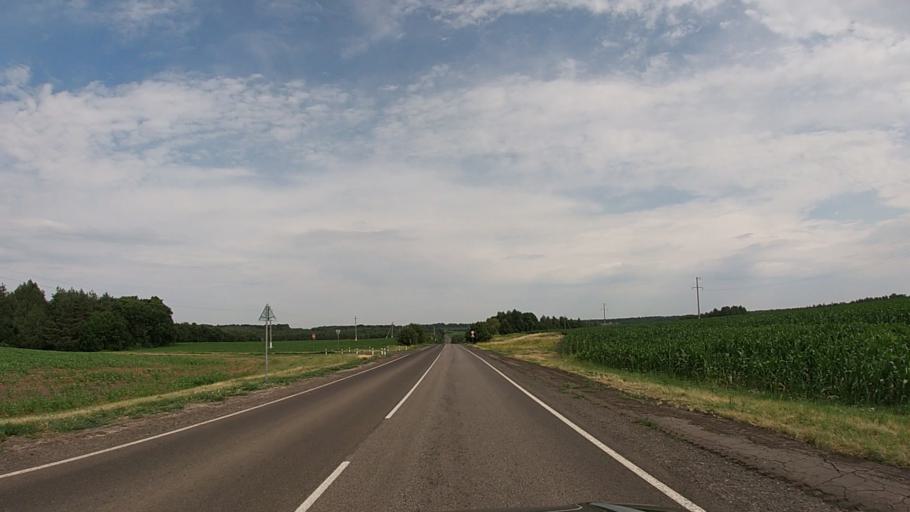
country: RU
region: Belgorod
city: Krasnaya Yaruga
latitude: 50.8216
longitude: 35.5013
